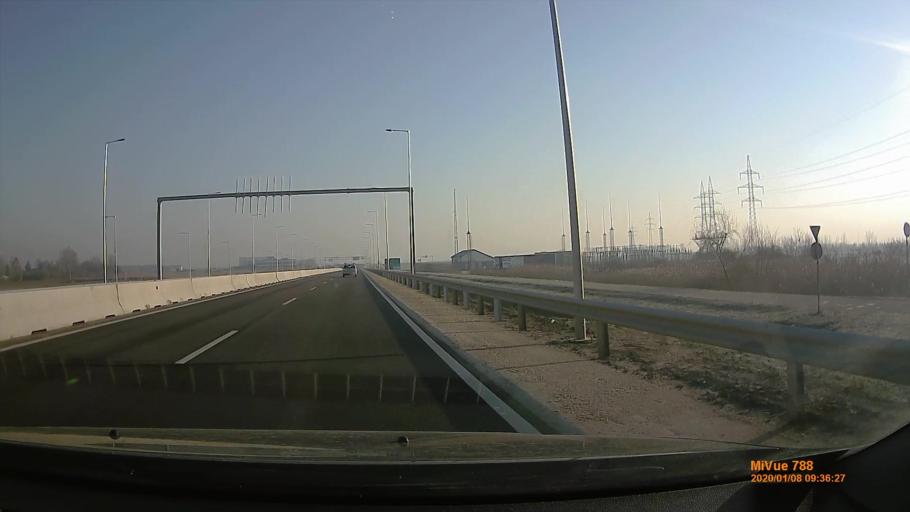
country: HU
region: Bacs-Kiskun
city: Kecskemet
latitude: 46.8772
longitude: 19.7024
